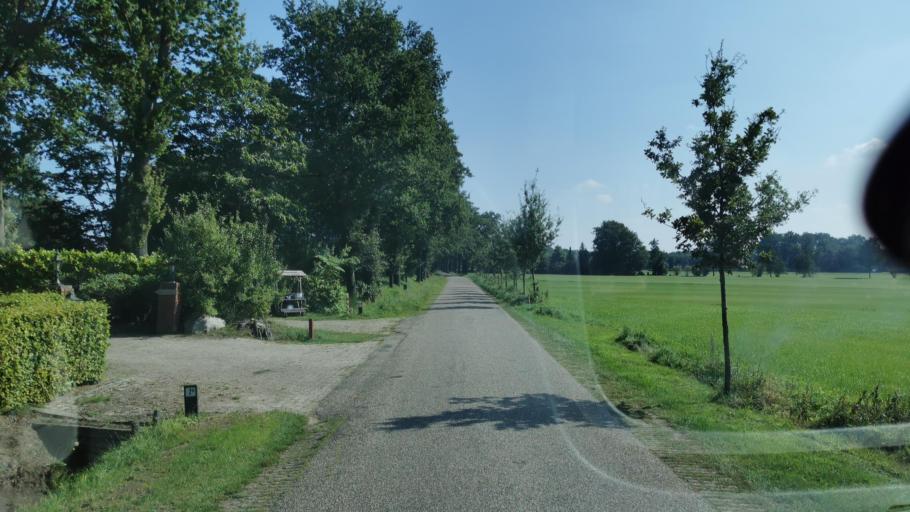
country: NL
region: Overijssel
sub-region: Gemeente Oldenzaal
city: Oldenzaal
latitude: 52.3275
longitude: 6.8906
